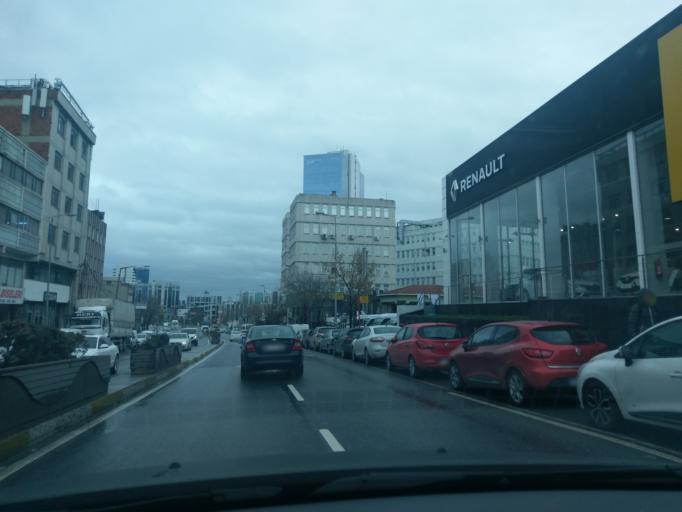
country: TR
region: Istanbul
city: Mahmutbey
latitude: 41.0607
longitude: 28.8321
